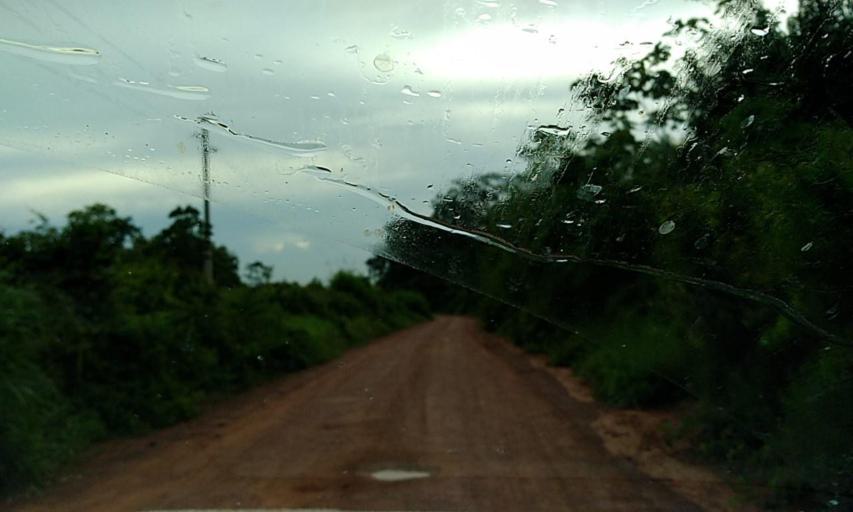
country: BR
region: Para
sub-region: Senador Jose Porfirio
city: Senador Jose Porfirio
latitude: -2.5532
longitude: -51.8677
